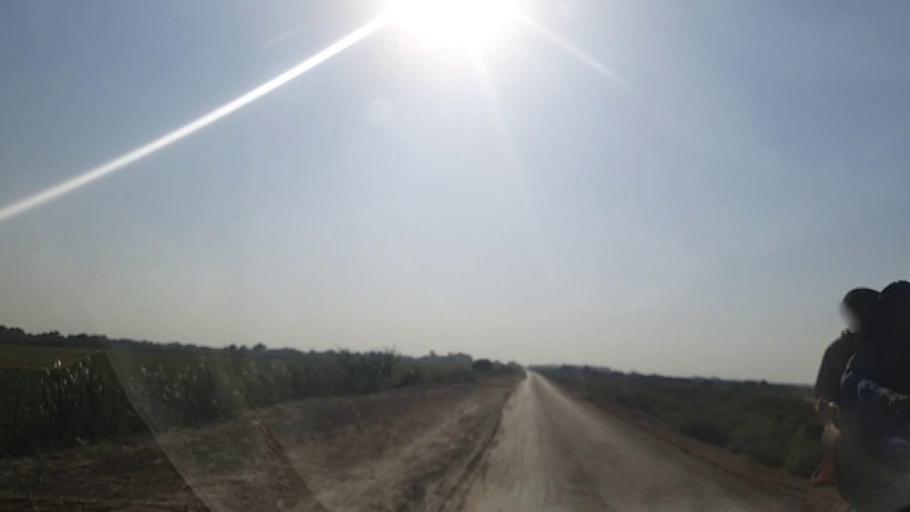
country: PK
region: Sindh
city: Mirpur Batoro
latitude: 24.5464
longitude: 68.1559
